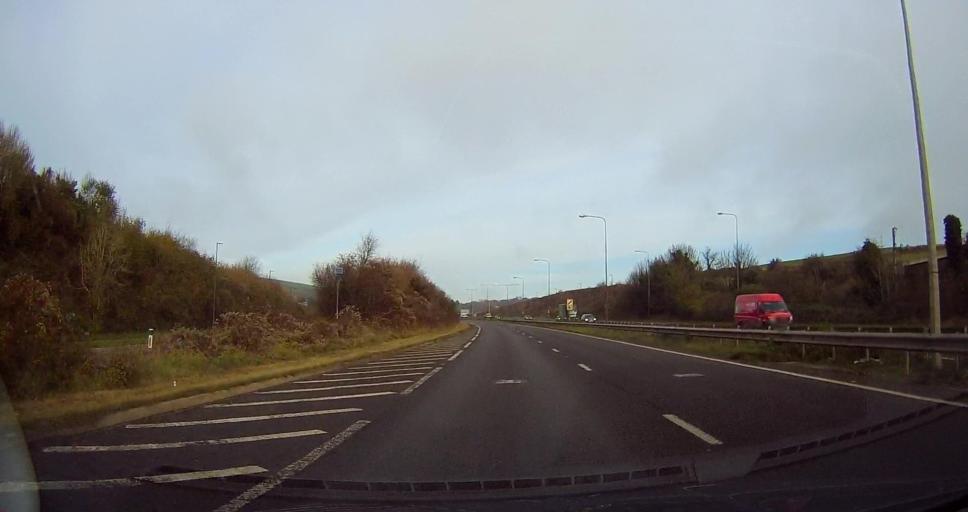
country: GB
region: England
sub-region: West Sussex
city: Hassocks
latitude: 50.8906
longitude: -0.1631
